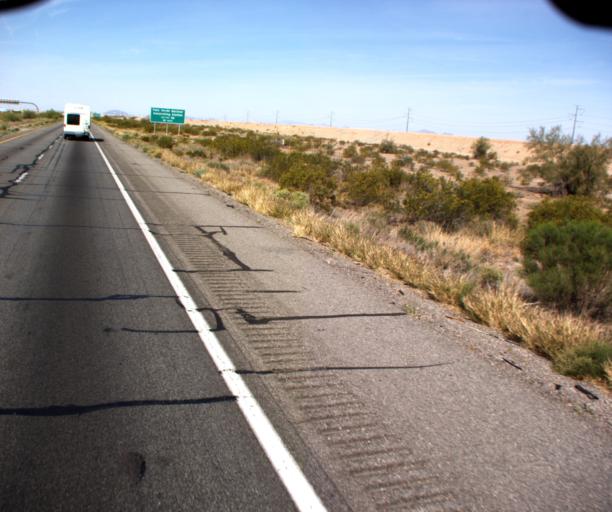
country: US
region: Arizona
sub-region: Maricopa County
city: Buckeye
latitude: 33.4363
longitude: -112.6635
